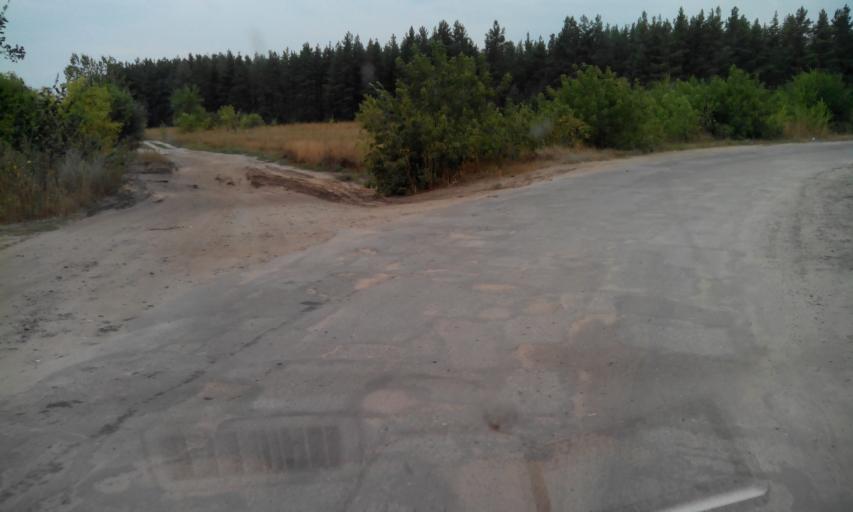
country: RU
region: Samara
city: Balasheyka
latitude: 53.1698
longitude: 48.1400
